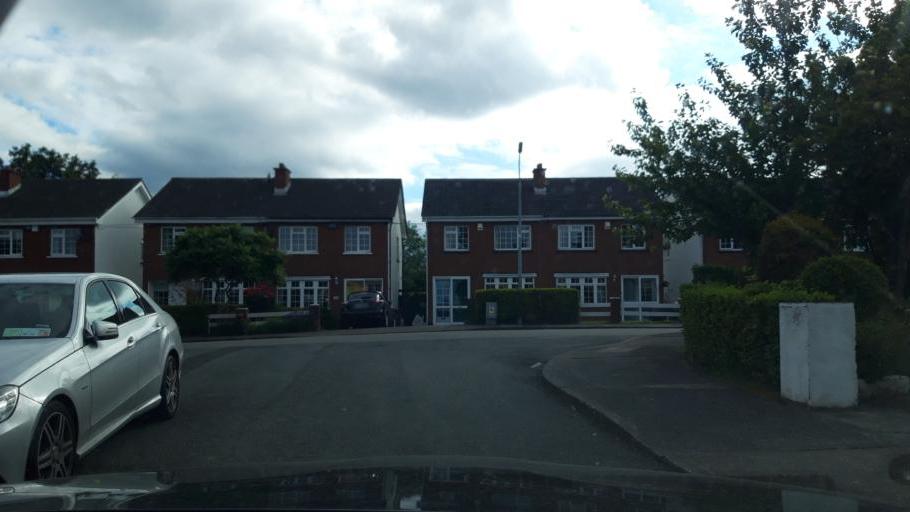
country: IE
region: Leinster
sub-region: Wicklow
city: Kilmacanoge
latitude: 53.1858
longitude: -6.1325
